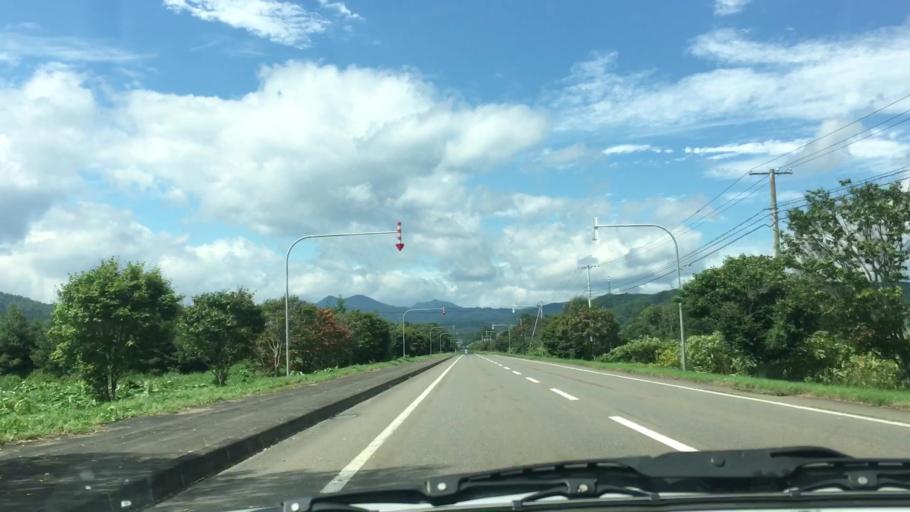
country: JP
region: Hokkaido
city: Otofuke
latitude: 43.3106
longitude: 143.3083
